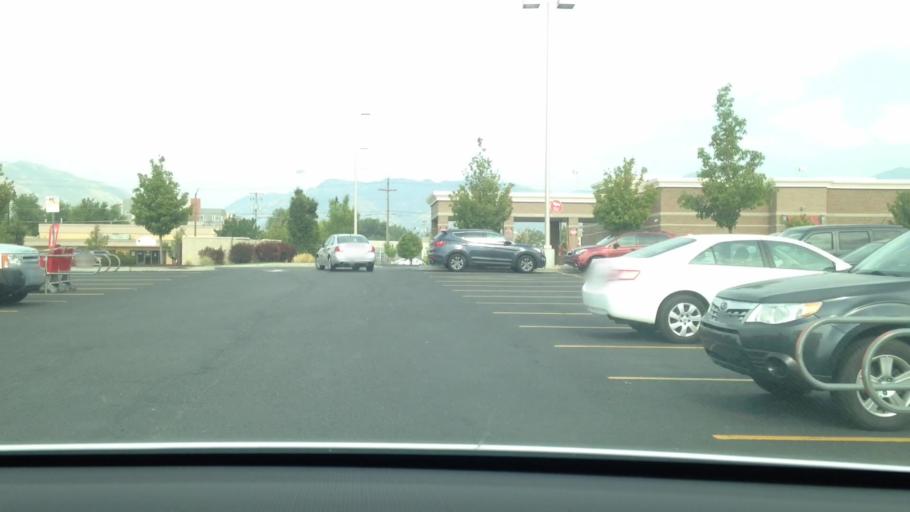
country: US
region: Utah
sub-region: Salt Lake County
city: Salt Lake City
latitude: 40.7453
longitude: -111.9011
